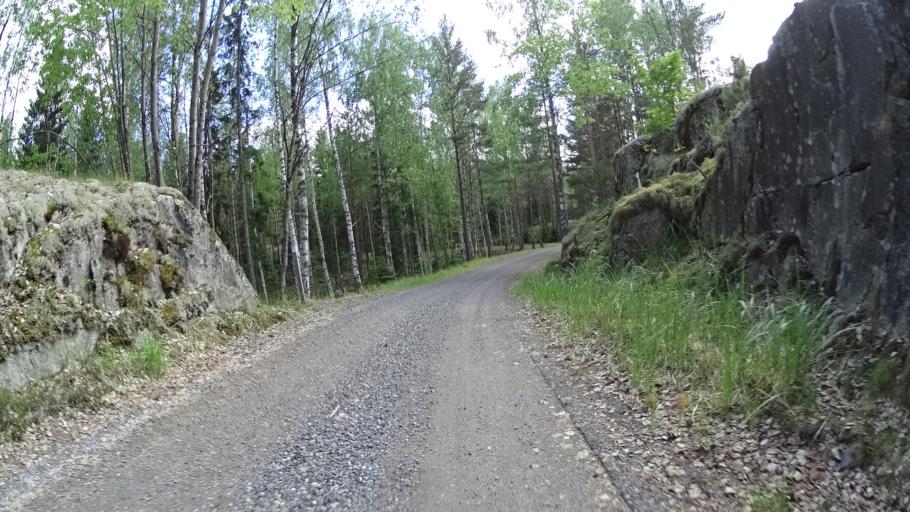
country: FI
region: Varsinais-Suomi
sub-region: Salo
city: Kisko
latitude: 60.1794
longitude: 23.5222
